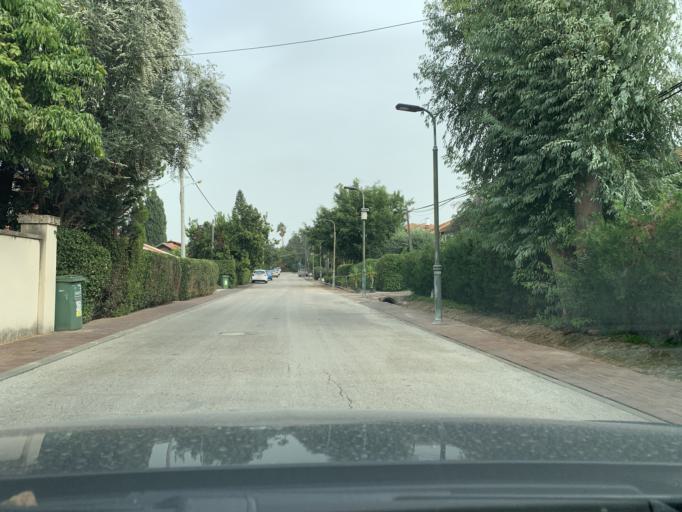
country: IL
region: Central District
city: Jaljulya
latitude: 32.1606
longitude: 34.9413
